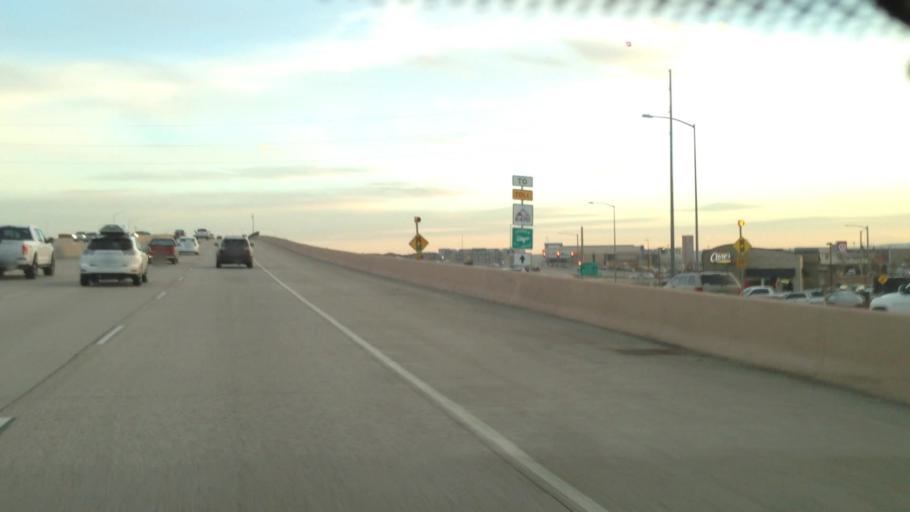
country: US
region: Colorado
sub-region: Arapahoe County
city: Dove Valley
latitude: 39.5970
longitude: -104.8035
